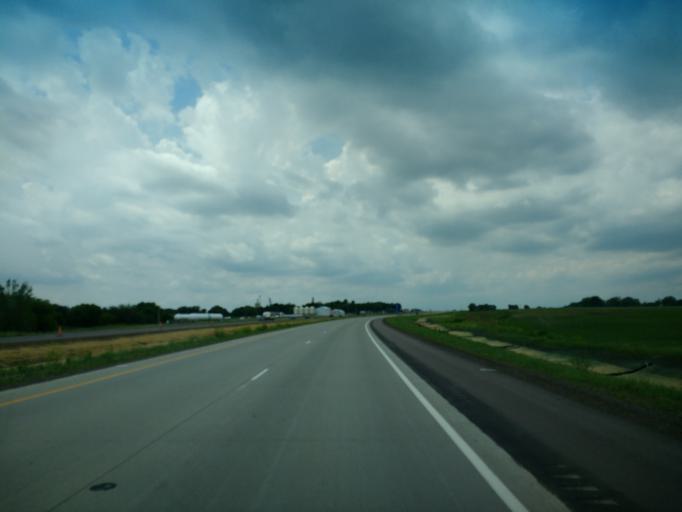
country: US
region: Minnesota
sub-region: Cottonwood County
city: Windom
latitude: 43.9106
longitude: -95.0306
